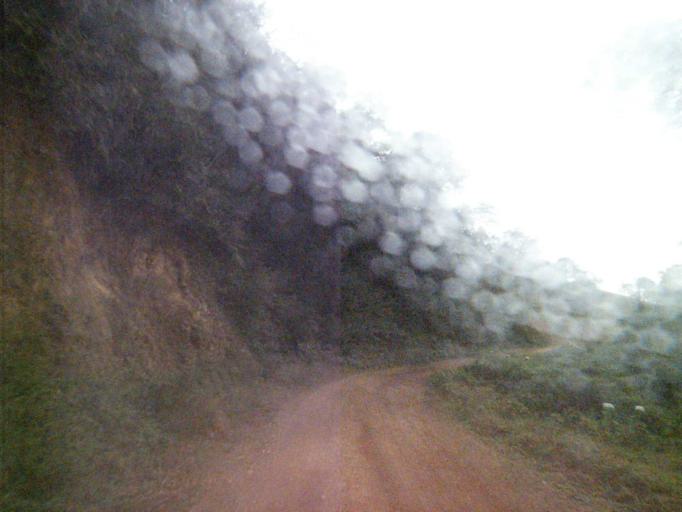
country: BR
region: Santa Catarina
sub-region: Anitapolis
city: Anitapolis
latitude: -27.8621
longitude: -49.1316
